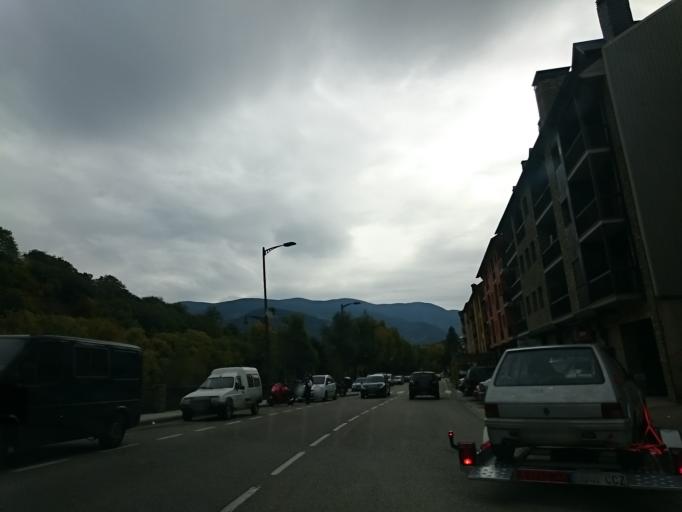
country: ES
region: Catalonia
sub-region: Provincia de Lleida
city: Sort
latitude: 42.4139
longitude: 1.1326
